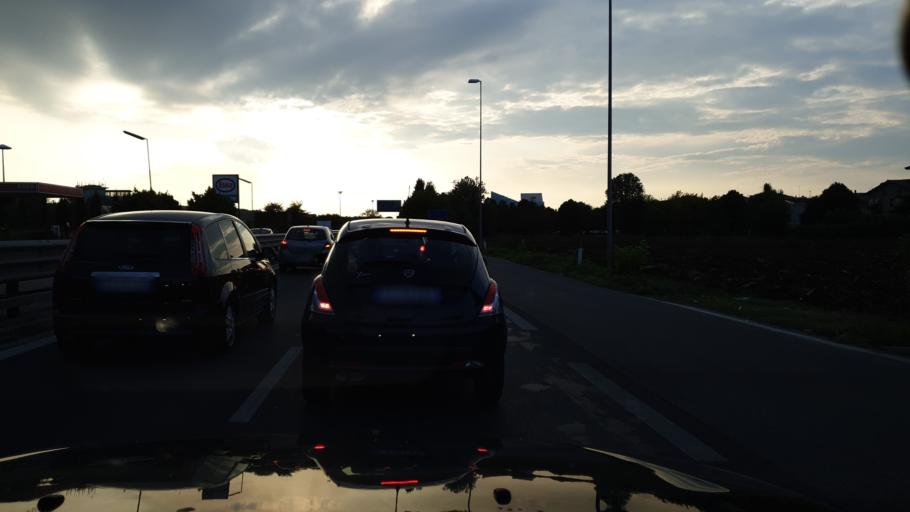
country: IT
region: Emilia-Romagna
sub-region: Provincia di Rimini
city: Rimini
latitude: 44.0417
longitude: 12.5795
